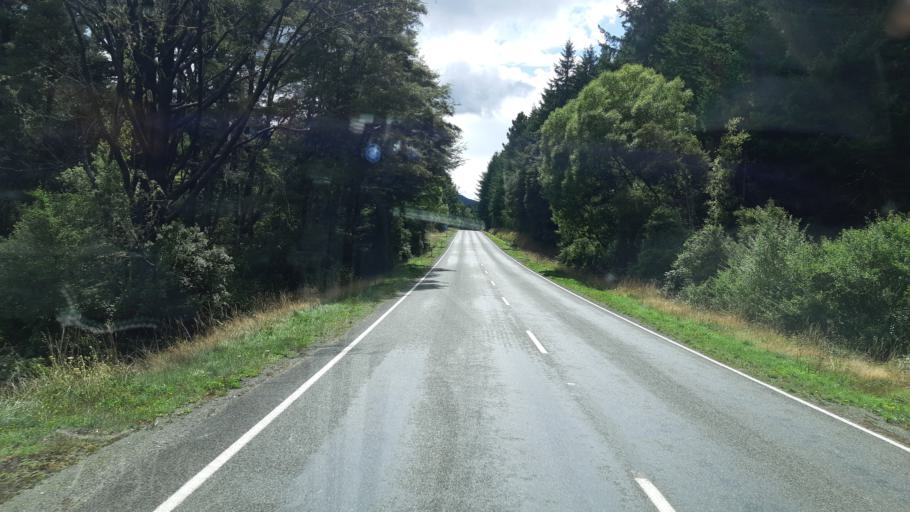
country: NZ
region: Tasman
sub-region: Tasman District
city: Wakefield
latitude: -41.5820
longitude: 172.7678
